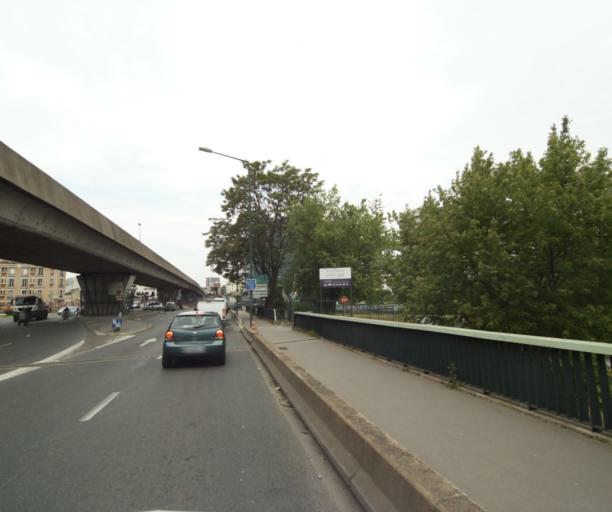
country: FR
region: Ile-de-France
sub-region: Departement des Hauts-de-Seine
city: Clichy
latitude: 48.9104
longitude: 2.2992
